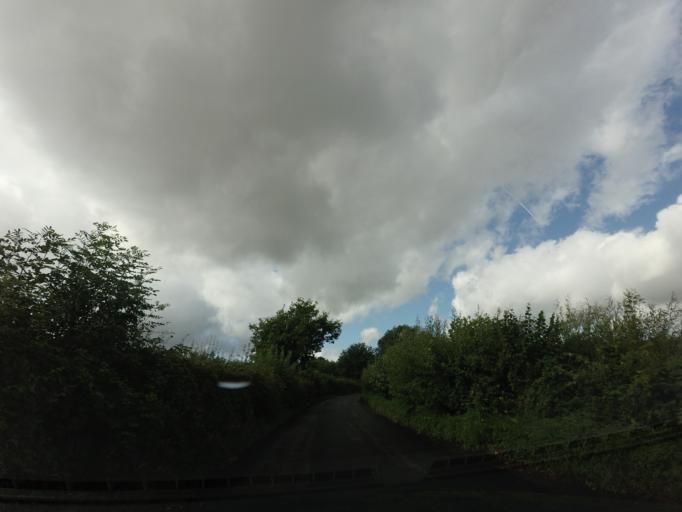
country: GB
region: England
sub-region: Kent
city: Paddock Wood
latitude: 51.1888
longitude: 0.3956
